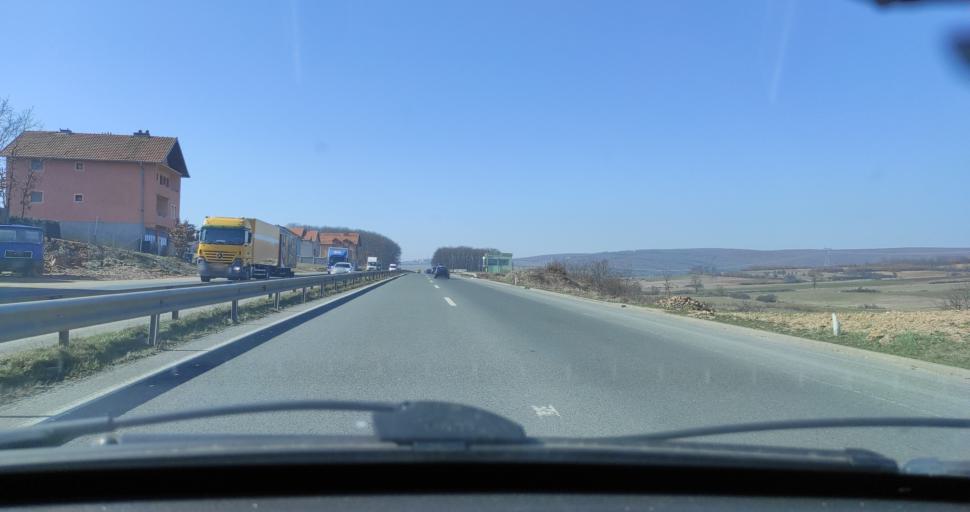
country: XK
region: Pristina
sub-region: Komuna e Drenasit
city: Glogovac
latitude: 42.5704
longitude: 20.8457
